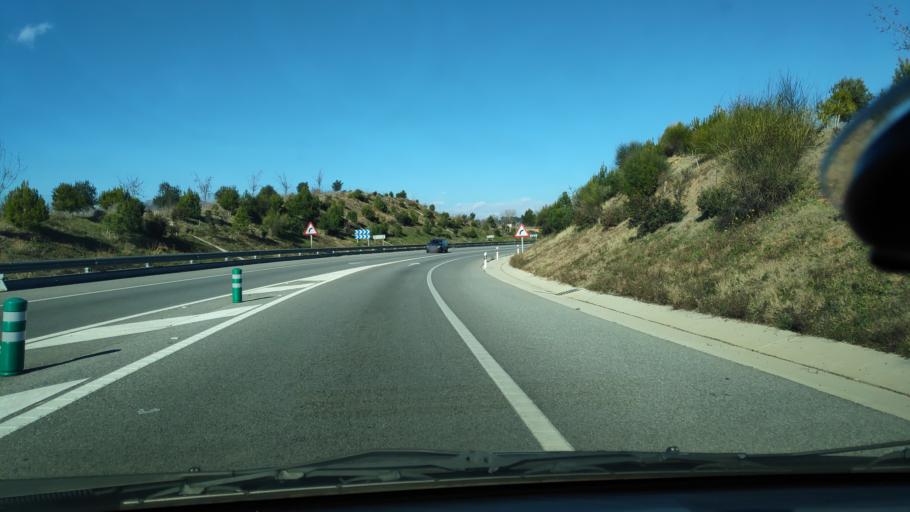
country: ES
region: Catalonia
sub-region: Provincia de Barcelona
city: Sant Quirze del Valles
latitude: 41.5689
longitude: 2.0760
